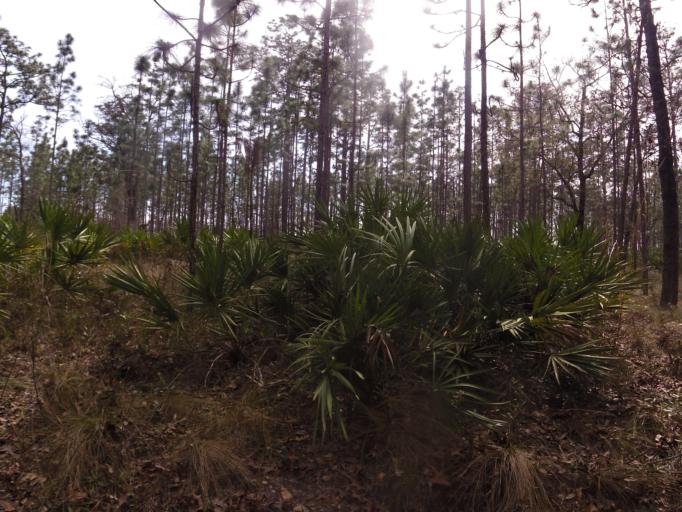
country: US
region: Florida
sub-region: Clay County
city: Middleburg
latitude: 30.1266
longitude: -81.8887
